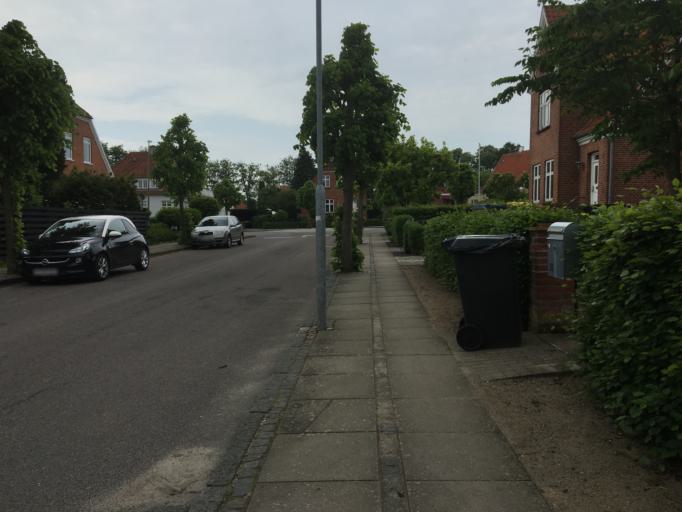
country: DK
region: South Denmark
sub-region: Middelfart Kommune
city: Middelfart
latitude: 55.5046
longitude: 9.7209
